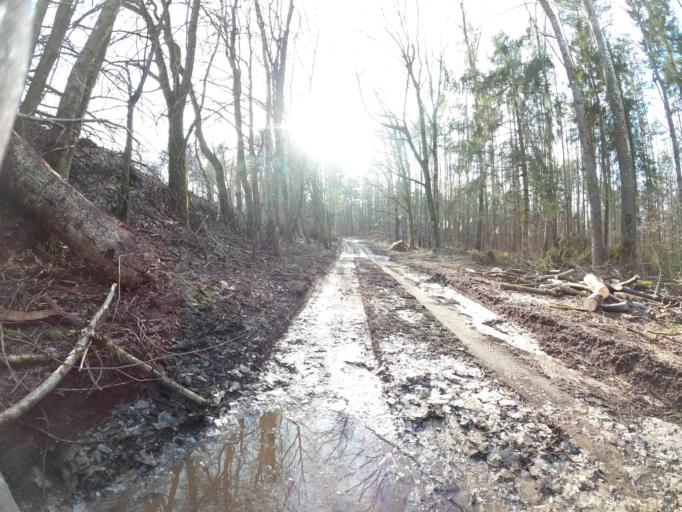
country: PL
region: West Pomeranian Voivodeship
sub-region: Powiat koszalinski
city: Polanow
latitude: 54.2323
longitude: 16.6394
